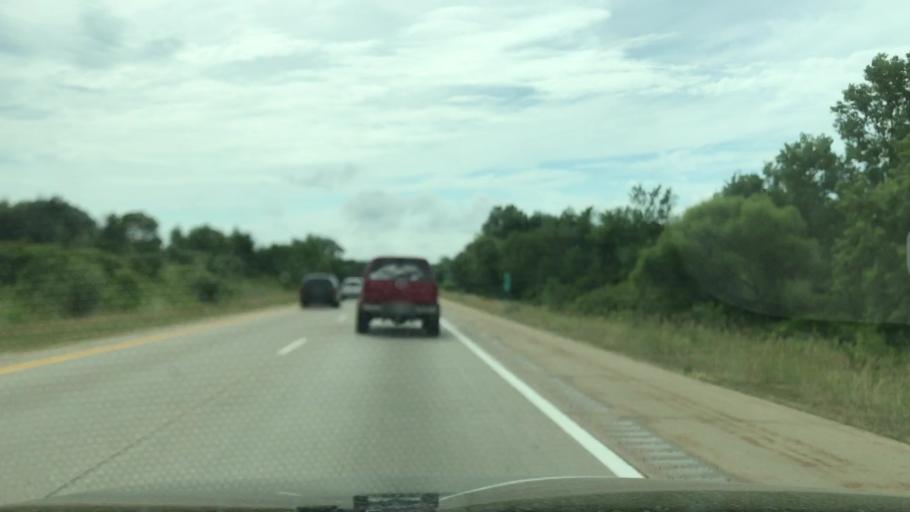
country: US
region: Michigan
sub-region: Kent County
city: Walker
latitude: 43.0181
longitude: -85.7512
